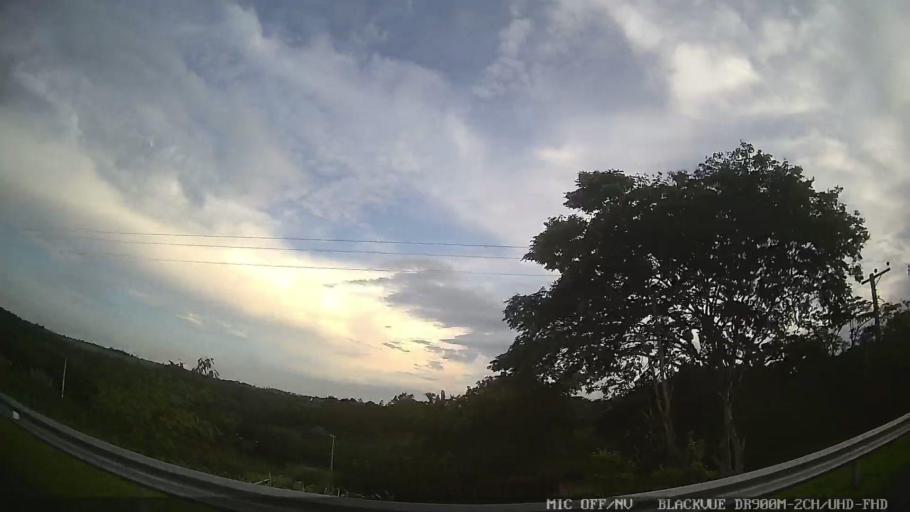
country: BR
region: Sao Paulo
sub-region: Porto Feliz
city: Porto Feliz
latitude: -23.2101
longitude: -47.5885
